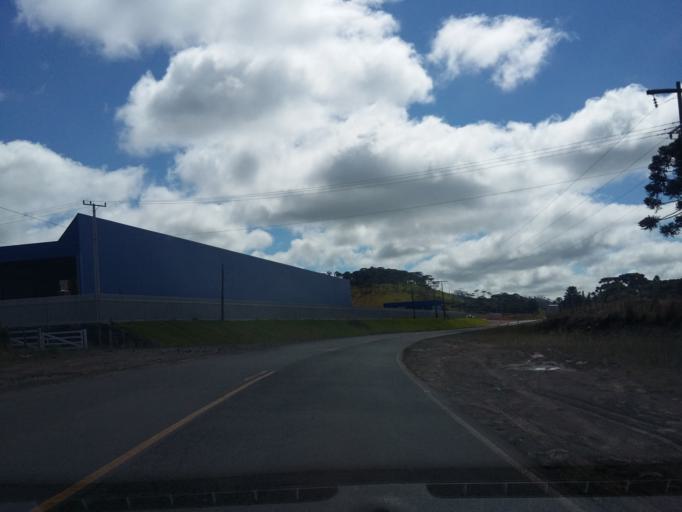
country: BR
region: Santa Catarina
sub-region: Sao Joaquim
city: Sao Joaquim
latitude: -28.2482
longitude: -49.8863
